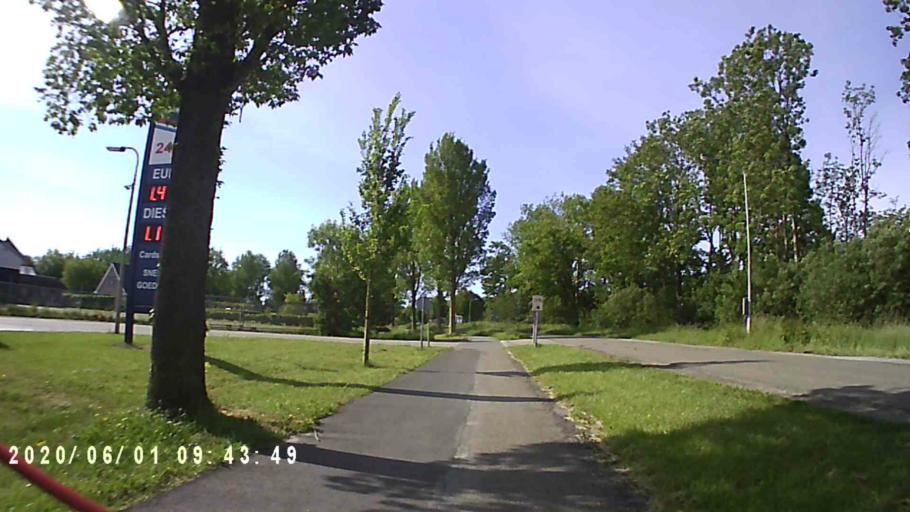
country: NL
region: Friesland
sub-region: Menameradiel
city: Menaam
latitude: 53.2396
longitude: 5.6839
